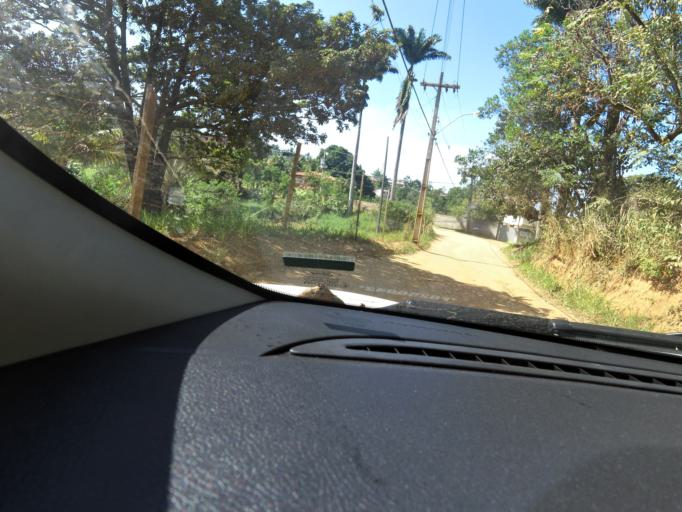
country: BR
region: Espirito Santo
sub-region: Guarapari
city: Guarapari
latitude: -20.6484
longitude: -40.5178
